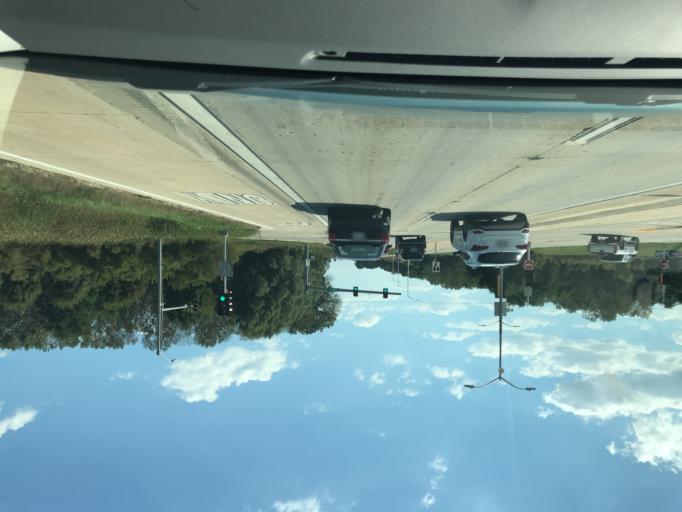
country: US
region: Wisconsin
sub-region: Kenosha County
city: Powers Lake
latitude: 42.5813
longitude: -88.2560
